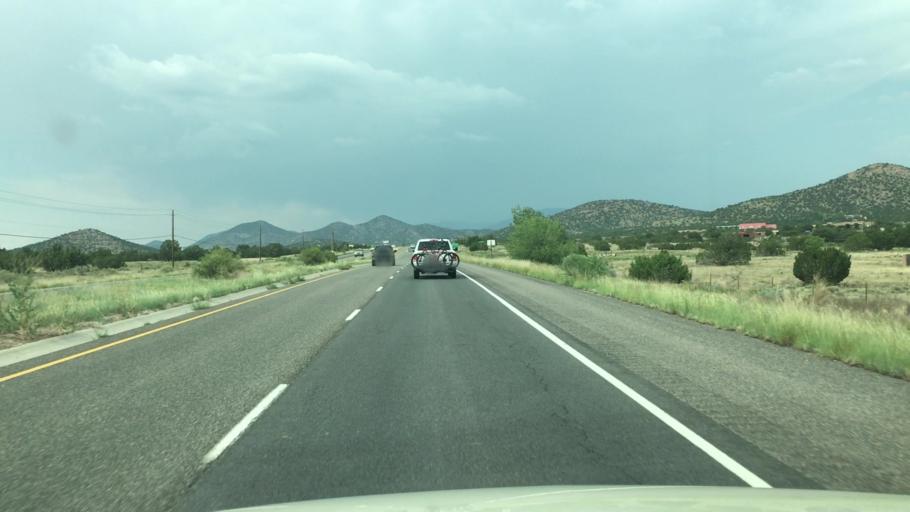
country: US
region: New Mexico
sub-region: Santa Fe County
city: Eldorado at Santa Fe
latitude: 35.5260
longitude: -105.8909
